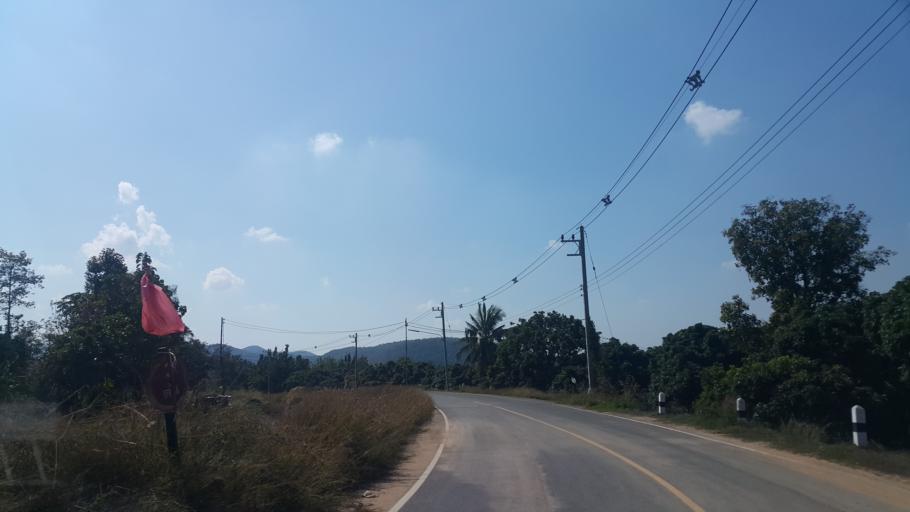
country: TH
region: Lamphun
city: Ban Thi
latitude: 18.6337
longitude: 99.1607
